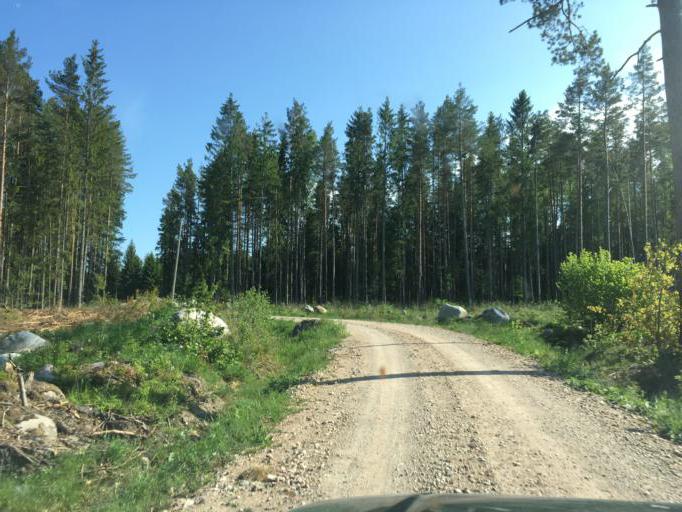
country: LV
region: Dundaga
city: Dundaga
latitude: 57.6133
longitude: 22.5028
